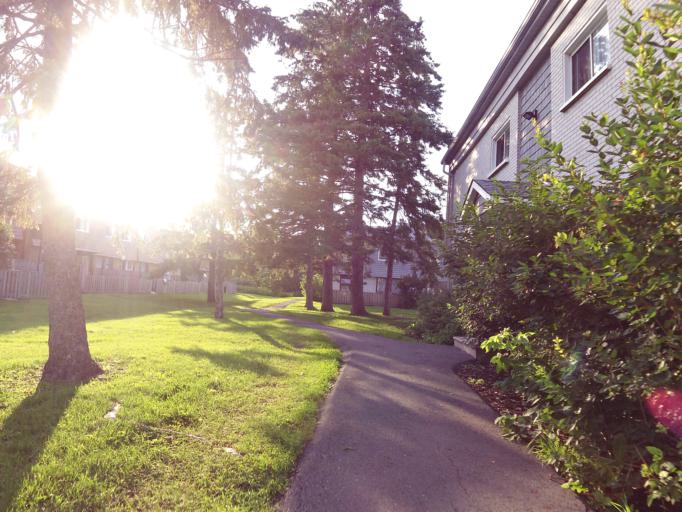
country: CA
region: Ontario
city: Bells Corners
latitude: 45.3493
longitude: -75.8132
